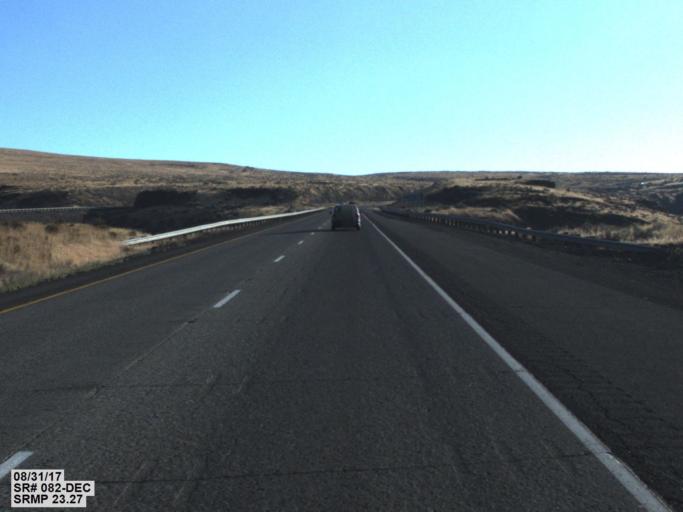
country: US
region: Washington
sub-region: Yakima County
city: Terrace Heights
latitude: 46.7091
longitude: -120.4322
